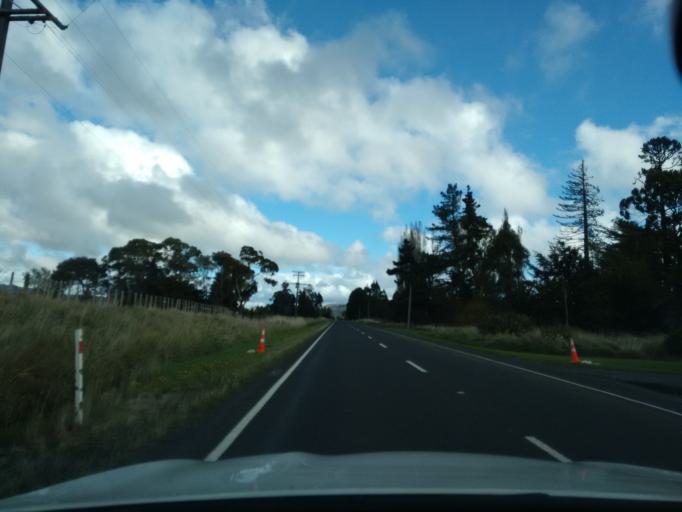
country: NZ
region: Manawatu-Wanganui
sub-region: Ruapehu District
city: Waiouru
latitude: -39.4033
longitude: 175.2853
